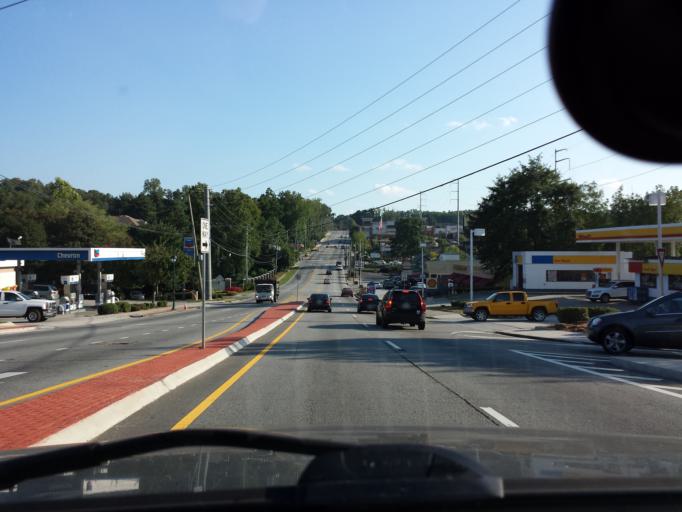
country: US
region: Georgia
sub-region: Fulton County
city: Sandy Springs
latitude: 33.9111
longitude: -84.3790
